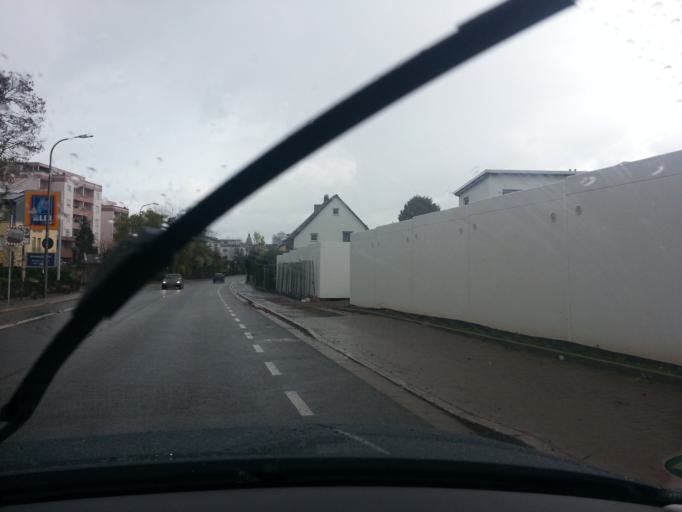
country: DE
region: Rheinland-Pfalz
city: Landau in der Pfalz
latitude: 49.1948
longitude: 8.1013
